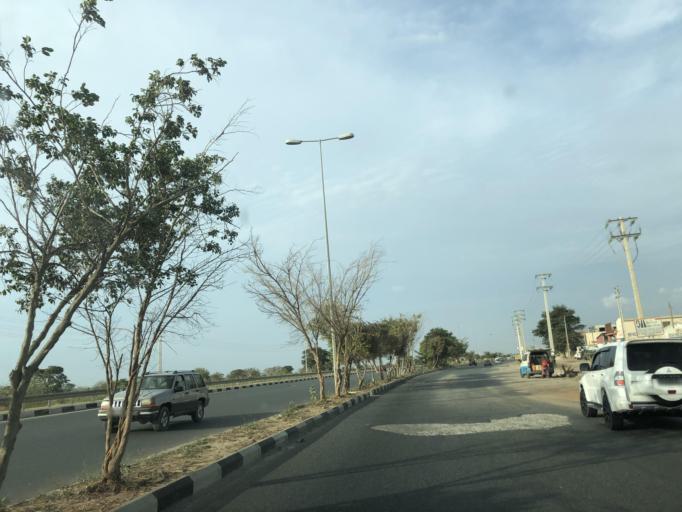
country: AO
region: Luanda
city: Luanda
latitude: -8.9391
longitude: 13.2955
